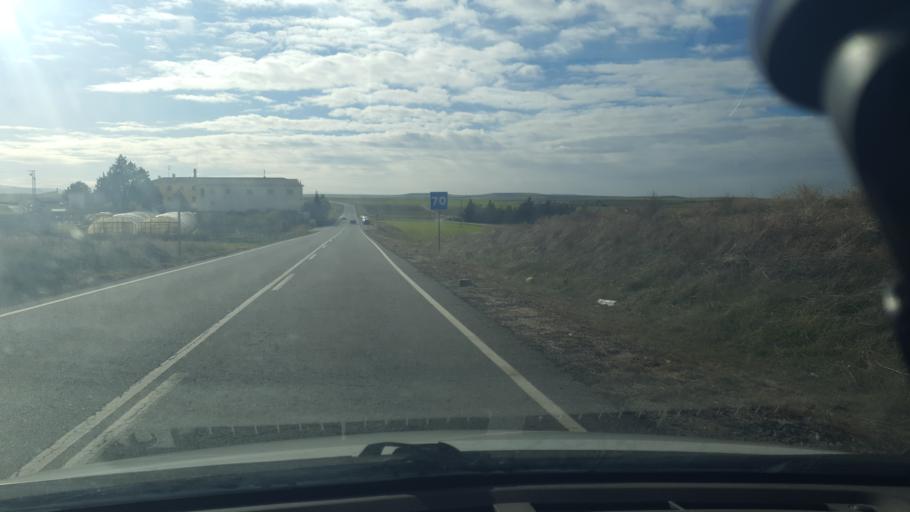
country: ES
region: Castille and Leon
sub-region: Provincia de Avila
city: Gotarrendura
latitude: 40.8235
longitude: -4.7407
